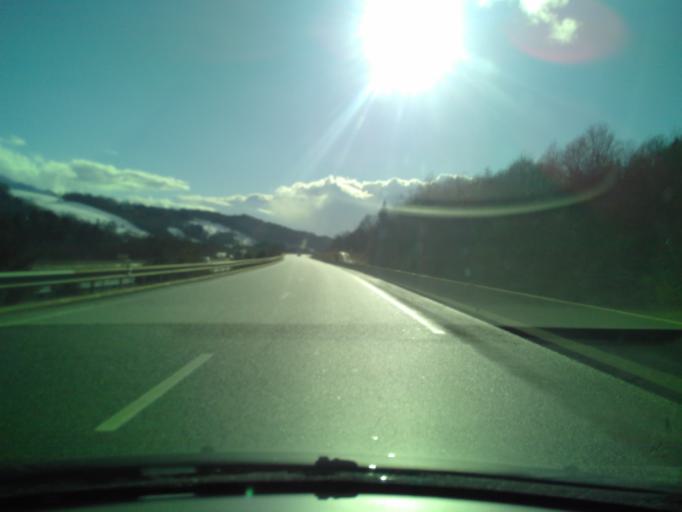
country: FR
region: Rhone-Alpes
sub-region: Departement de la Haute-Savoie
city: Evires
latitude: 46.0329
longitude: 6.2352
